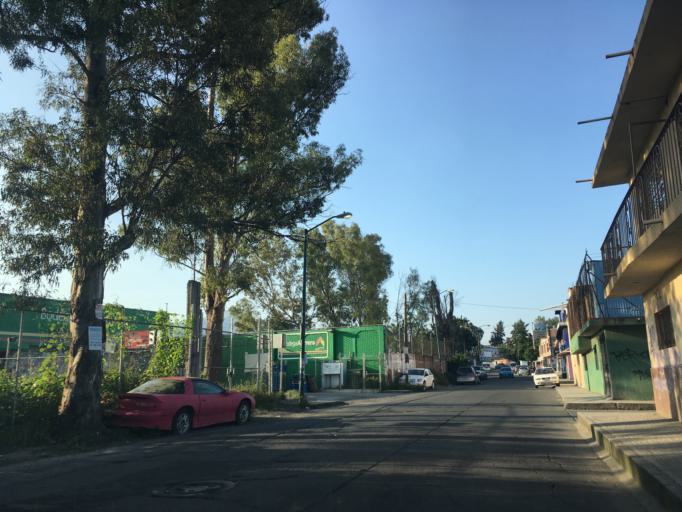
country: MX
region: Michoacan
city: Morelia
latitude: 19.6938
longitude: -101.2269
